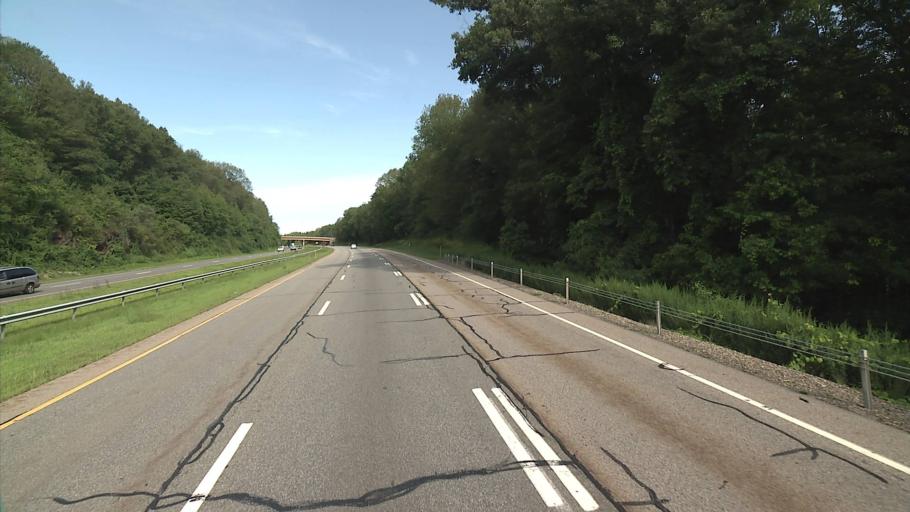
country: US
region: Connecticut
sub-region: New London County
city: Montville Center
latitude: 41.5682
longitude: -72.1792
